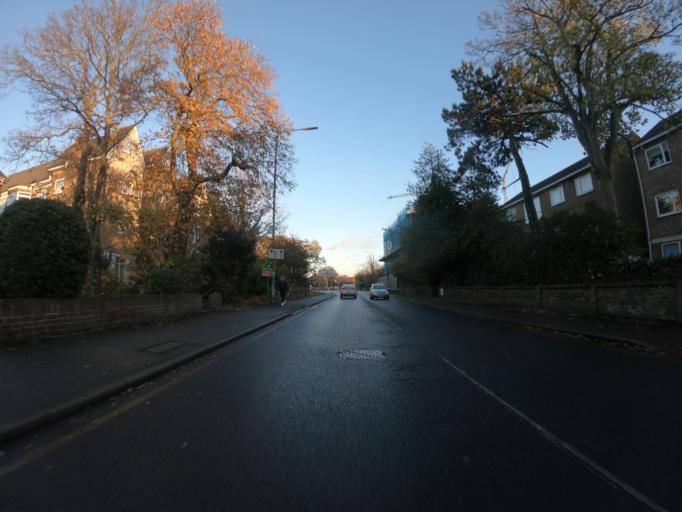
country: GB
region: England
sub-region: Greater London
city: Belvedere
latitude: 51.4842
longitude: 0.1466
